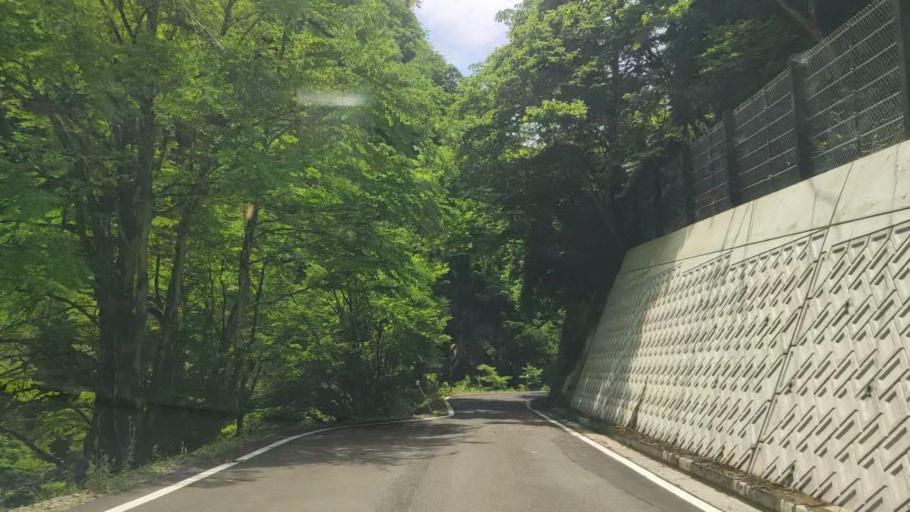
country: JP
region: Tottori
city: Tottori
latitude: 35.4087
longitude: 134.5065
